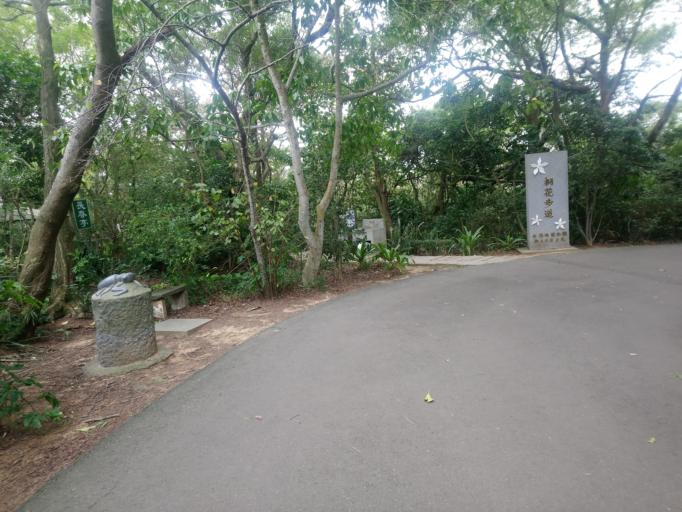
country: TW
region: Taiwan
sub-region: Hsinchu
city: Hsinchu
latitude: 24.7910
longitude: 120.9848
